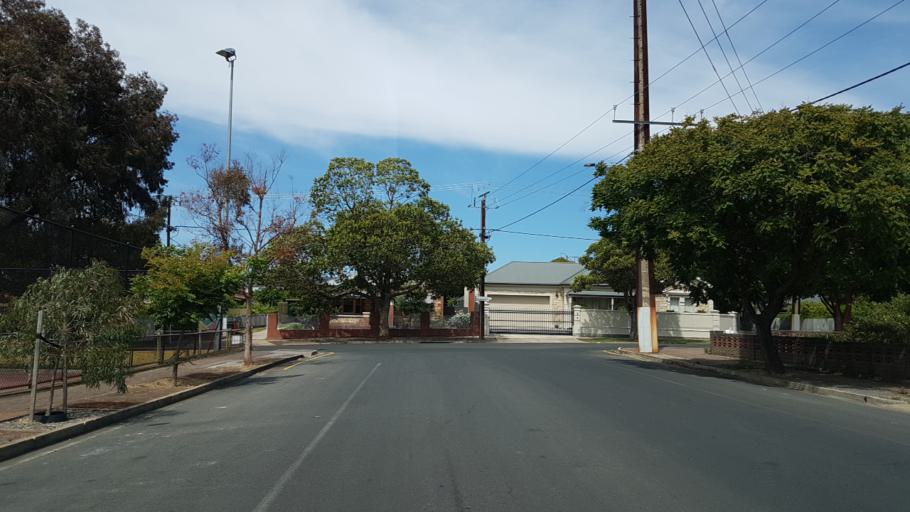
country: AU
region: South Australia
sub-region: Norwood Payneham St Peters
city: Trinity Gardens
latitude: -34.9118
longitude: 138.6481
